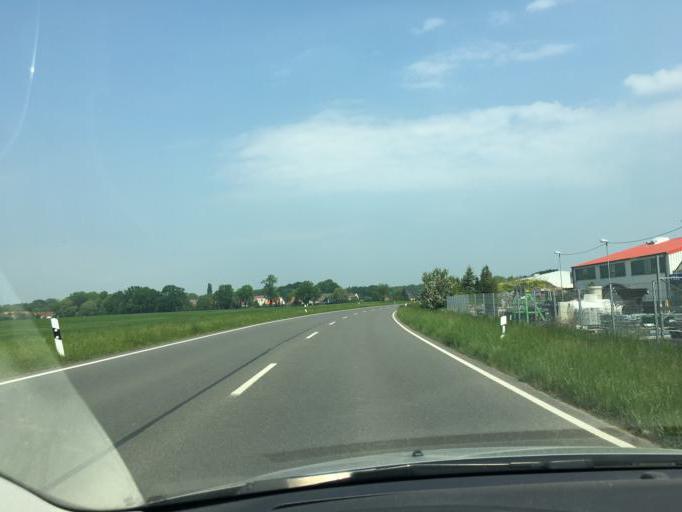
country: DE
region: Saxony
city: Naunhof
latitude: 51.2811
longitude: 12.5759
